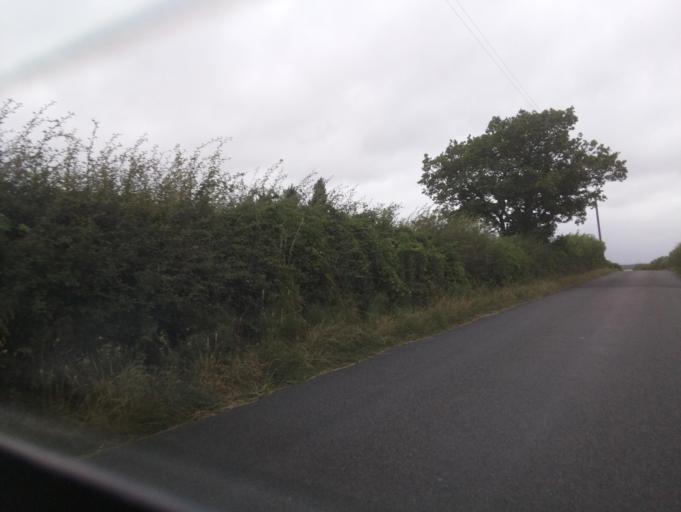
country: GB
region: England
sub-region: Leicestershire
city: Ashby de la Zouch
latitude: 52.7733
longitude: -1.5052
